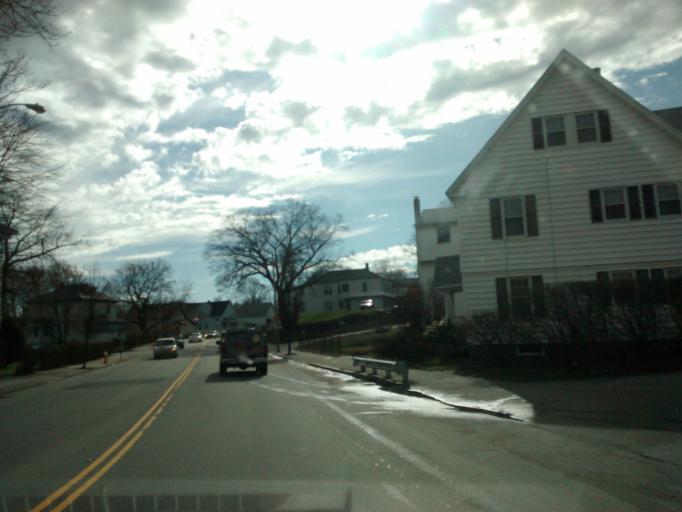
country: US
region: Massachusetts
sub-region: Worcester County
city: Sunderland
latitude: 42.2508
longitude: -71.7729
